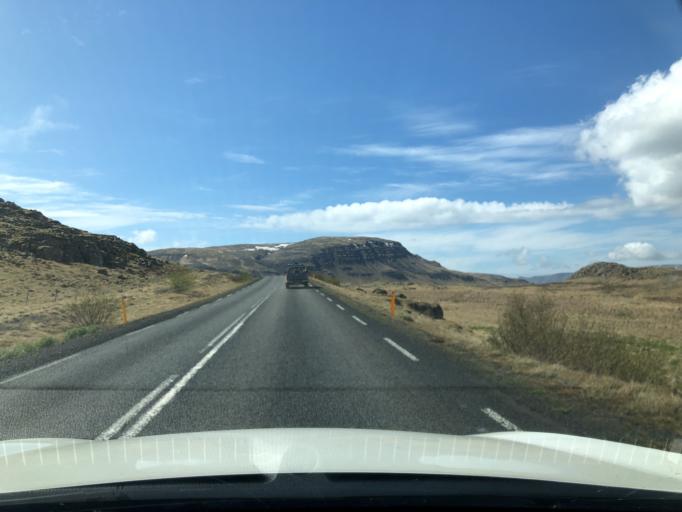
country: IS
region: Capital Region
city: Mosfellsbaer
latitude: 64.3345
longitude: -21.6239
